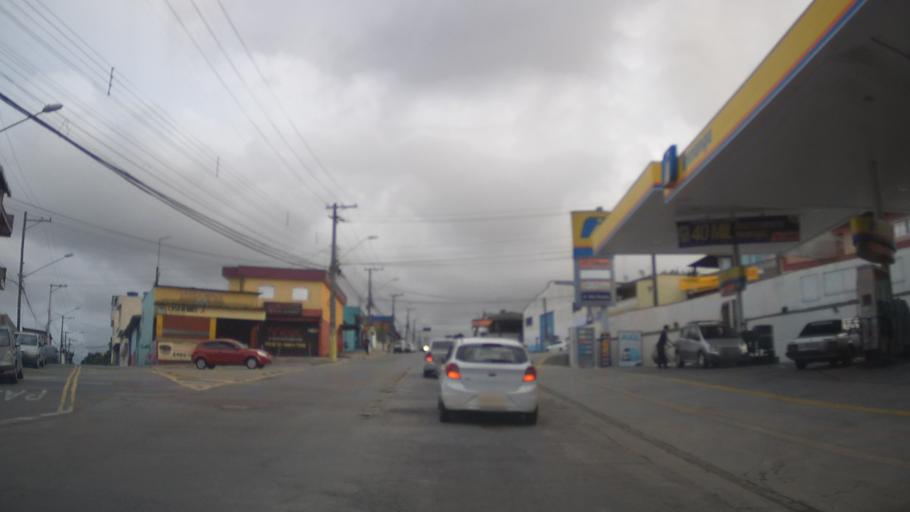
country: BR
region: Sao Paulo
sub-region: Itaquaquecetuba
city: Itaquaquecetuba
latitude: -23.4399
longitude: -46.4279
